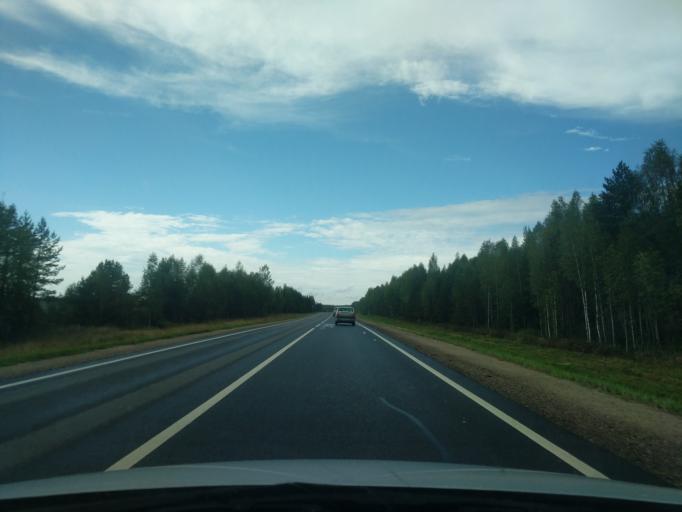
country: RU
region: Kostroma
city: Ostrovskoye
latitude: 57.8141
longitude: 42.0023
